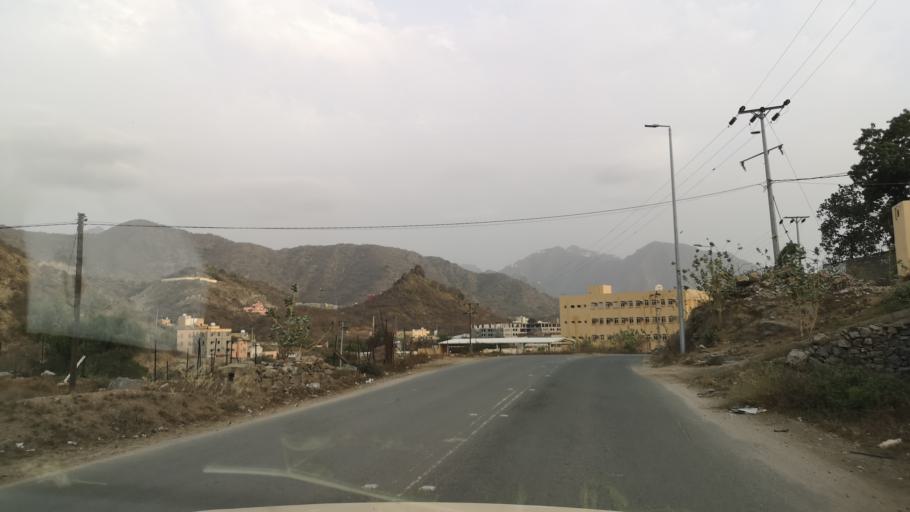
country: YE
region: Sa'dah
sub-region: Monabbih
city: Suq al Khamis
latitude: 17.3657
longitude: 43.1274
